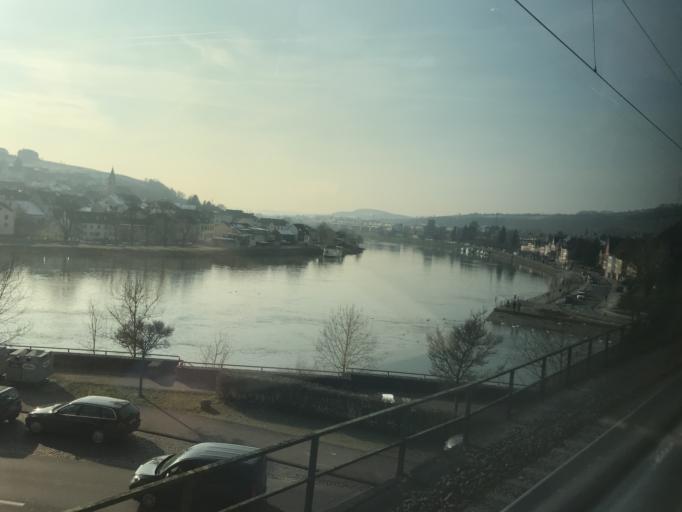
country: LU
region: Grevenmacher
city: Wasserbillig
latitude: 49.7135
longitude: 6.5085
